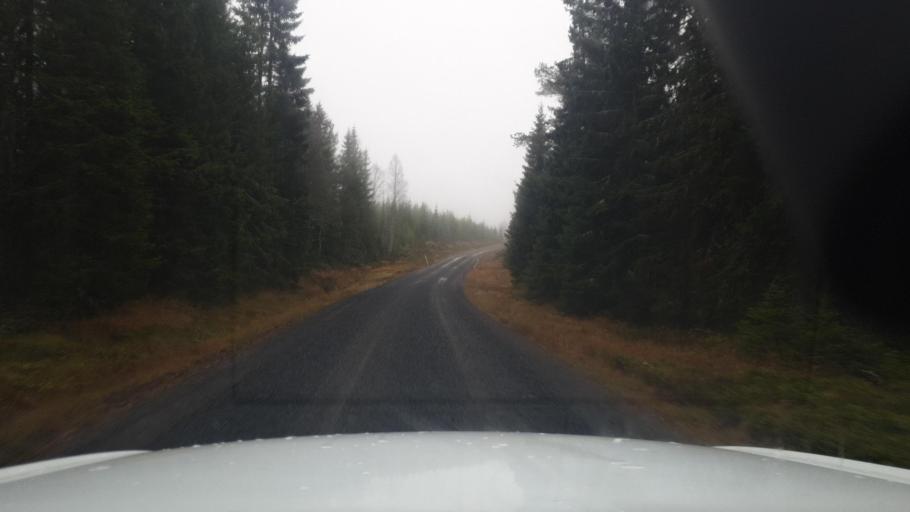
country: SE
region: Vaermland
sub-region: Eda Kommun
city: Charlottenberg
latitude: 60.1162
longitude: 12.6029
